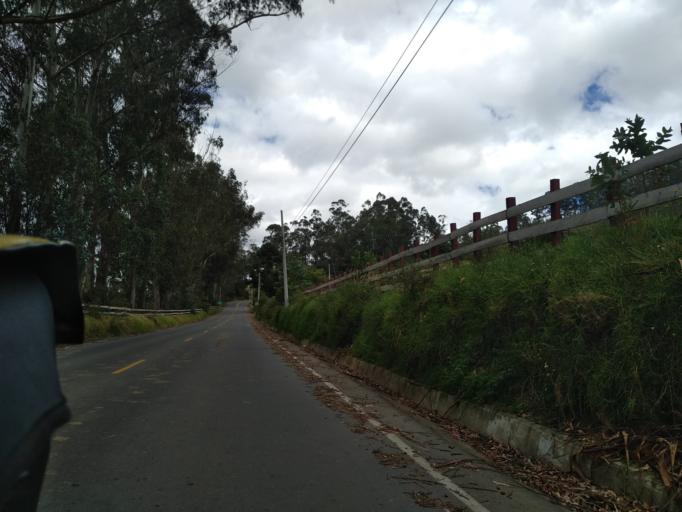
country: EC
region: Cotopaxi
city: Saquisili
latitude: -0.7186
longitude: -78.8871
